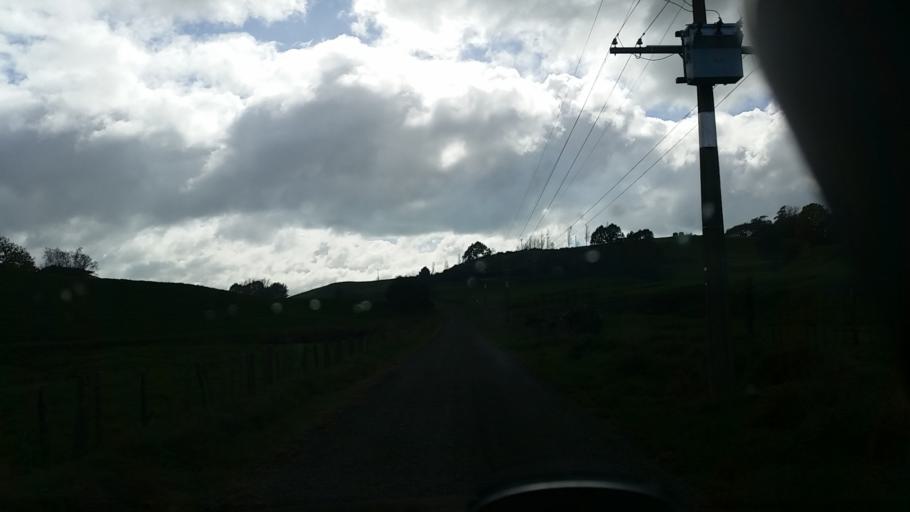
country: NZ
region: Waikato
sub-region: Matamata-Piako District
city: Matamata
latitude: -37.8131
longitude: 175.6733
